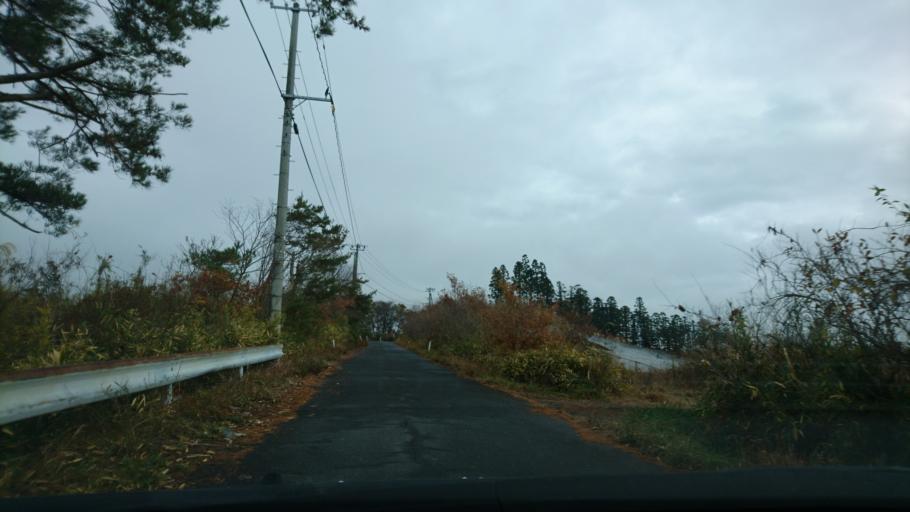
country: JP
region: Iwate
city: Ichinoseki
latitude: 38.8793
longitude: 141.1468
